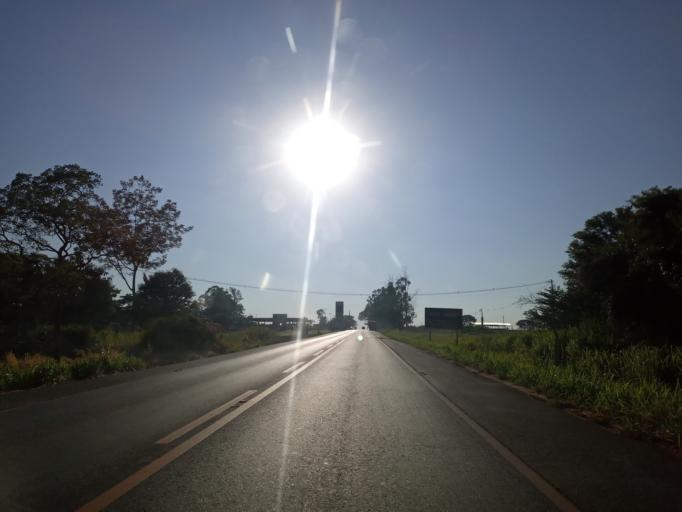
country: BR
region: Minas Gerais
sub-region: Ituiutaba
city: Ituiutaba
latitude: -18.9657
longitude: -49.5033
